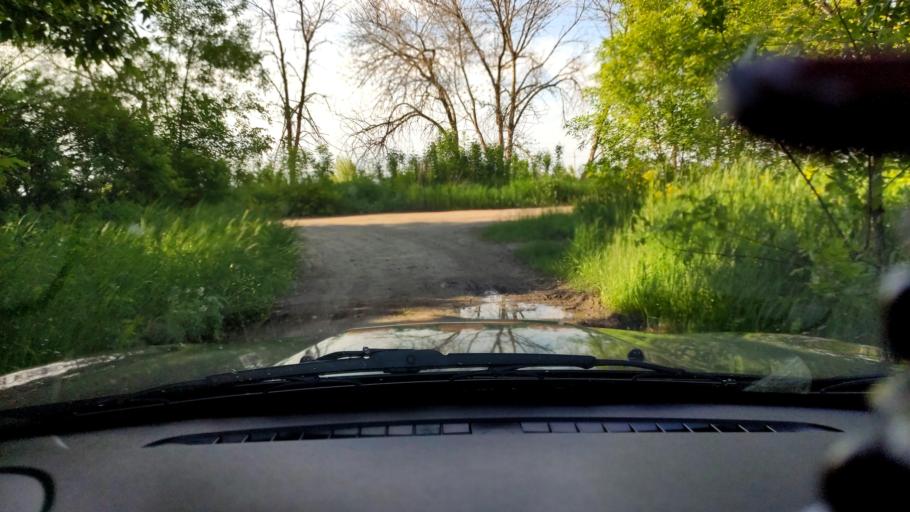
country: RU
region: Voronezj
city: Uryv-Pokrovka
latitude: 51.1218
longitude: 39.1784
